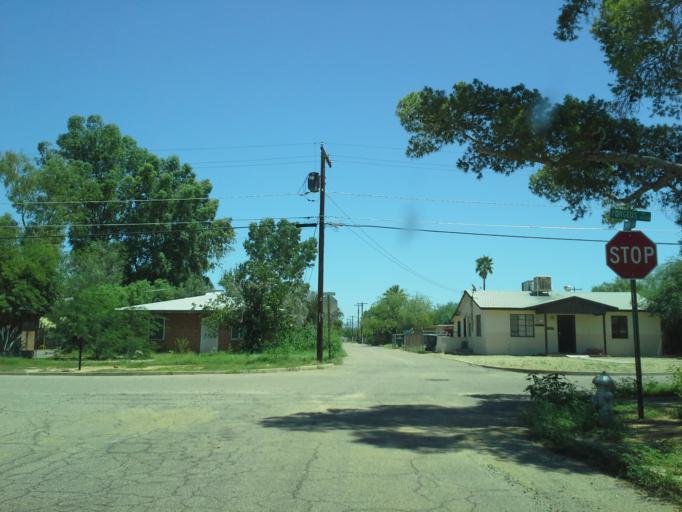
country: US
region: Arizona
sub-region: Pima County
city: Tucson
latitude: 32.2550
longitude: -110.9334
